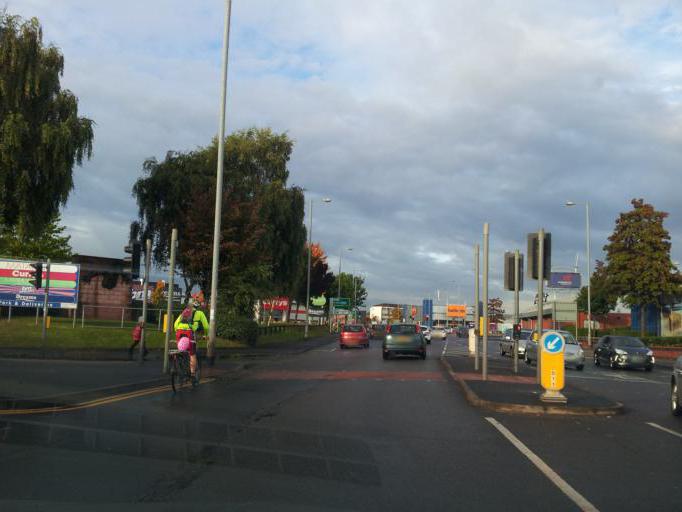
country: GB
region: England
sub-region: Manchester
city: Cheetham Hill
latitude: 53.4977
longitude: -2.2372
